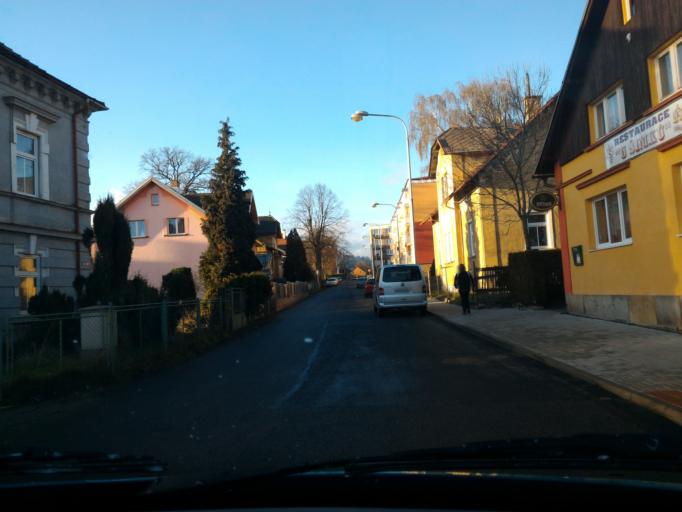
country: CZ
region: Ustecky
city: Varnsdorf
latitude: 50.9121
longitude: 14.6308
